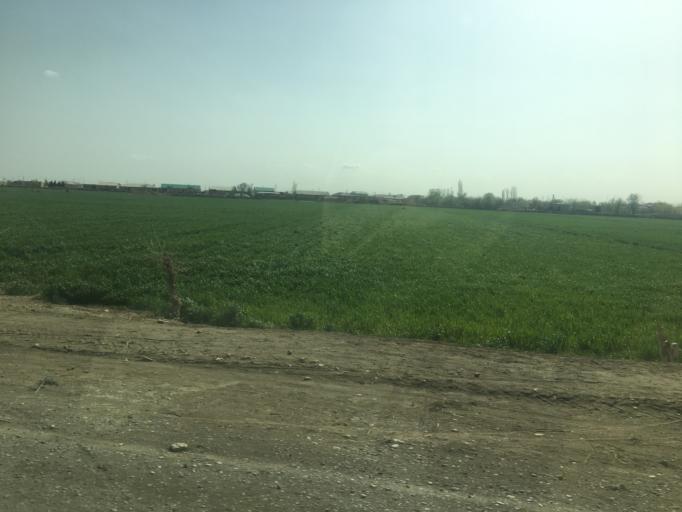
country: TM
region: Lebap
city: Farap
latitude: 39.2057
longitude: 63.5577
